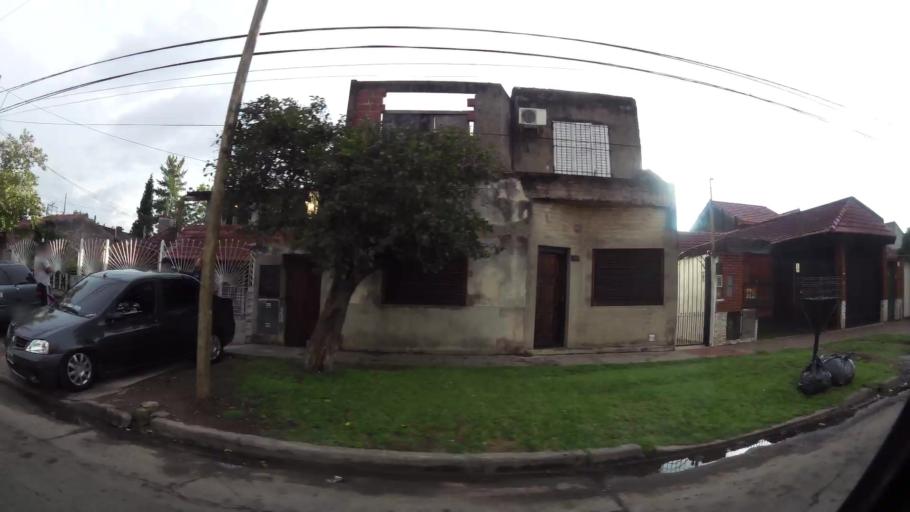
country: AR
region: Buenos Aires
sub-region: Partido de Lomas de Zamora
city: Lomas de Zamora
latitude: -34.7436
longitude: -58.3508
